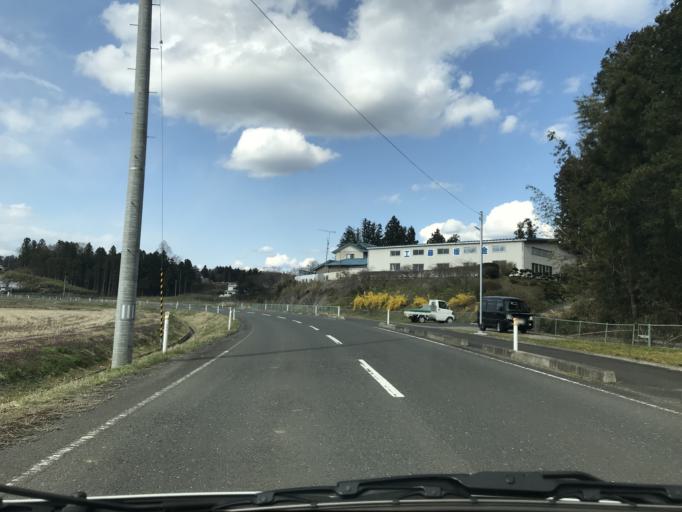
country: JP
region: Iwate
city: Ichinoseki
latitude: 38.7484
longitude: 141.1873
